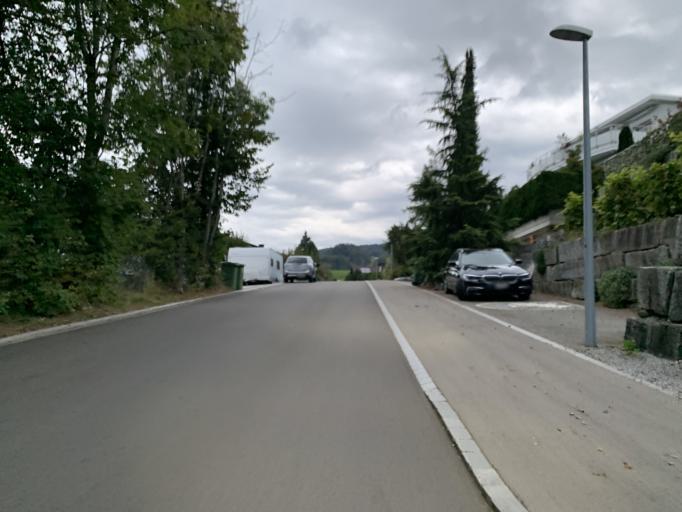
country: CH
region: Zurich
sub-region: Bezirk Hinwil
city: Hadlikon
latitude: 47.2986
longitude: 8.8610
